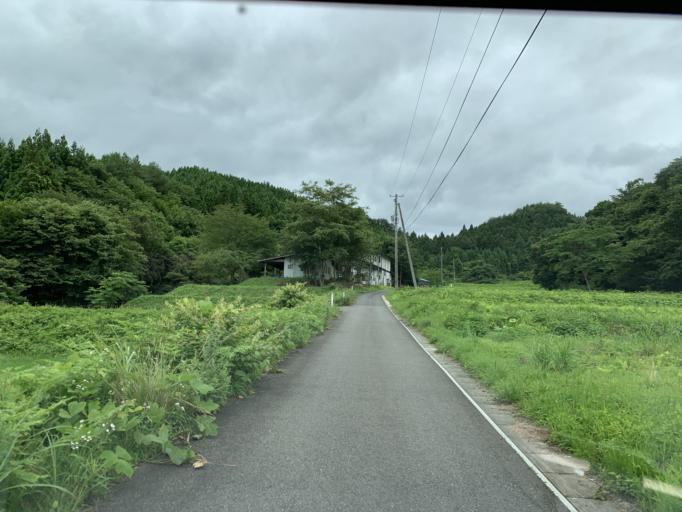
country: JP
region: Iwate
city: Ichinoseki
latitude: 38.8970
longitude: 140.9761
